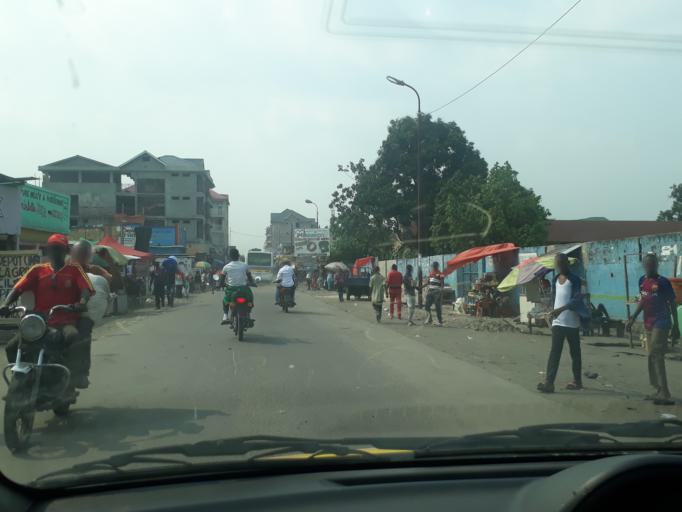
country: CD
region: Kinshasa
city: Kinshasa
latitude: -4.3132
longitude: 15.3187
